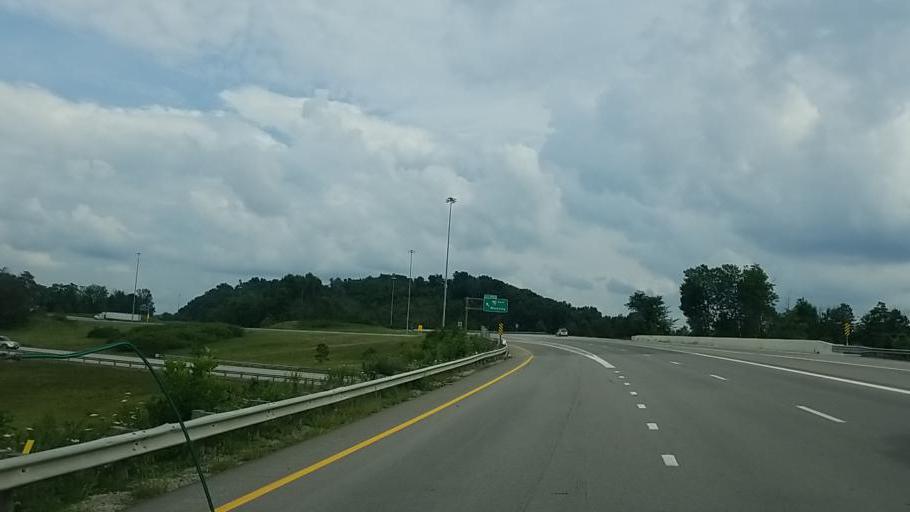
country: US
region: Ohio
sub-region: Guernsey County
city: Byesville
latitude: 39.9995
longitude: -81.5612
